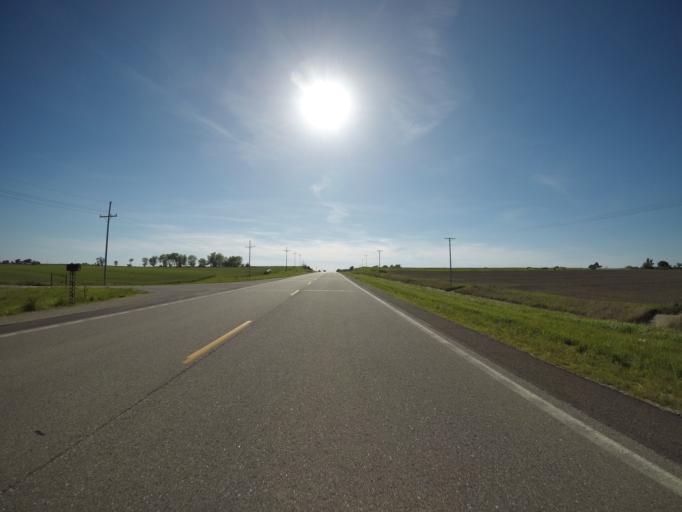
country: US
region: Kansas
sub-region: Clay County
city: Clay Center
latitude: 39.3647
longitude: -96.9168
